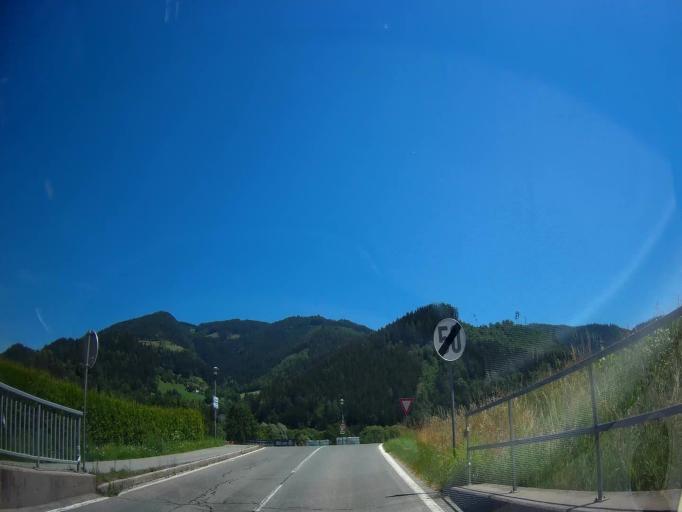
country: AT
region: Carinthia
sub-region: Politischer Bezirk Sankt Veit an der Glan
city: Micheldorf
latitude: 46.9136
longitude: 14.4323
